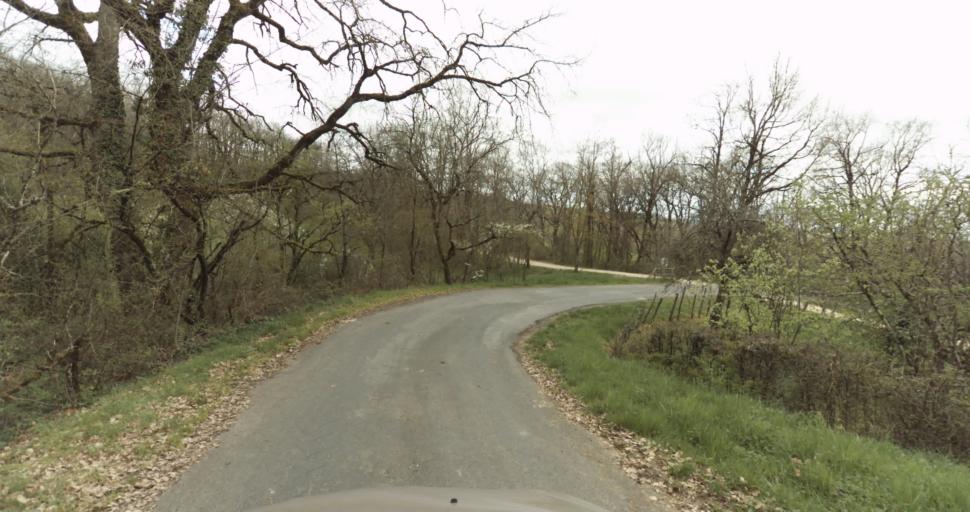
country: FR
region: Midi-Pyrenees
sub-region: Departement du Tarn
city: Puygouzon
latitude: 43.8669
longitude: 2.1806
